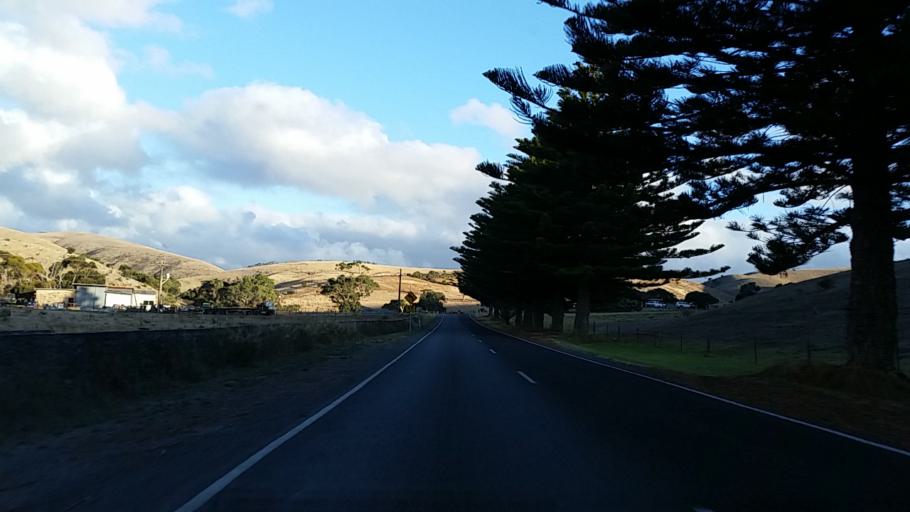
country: AU
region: South Australia
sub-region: Yankalilla
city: Normanville
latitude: -35.5297
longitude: 138.1913
